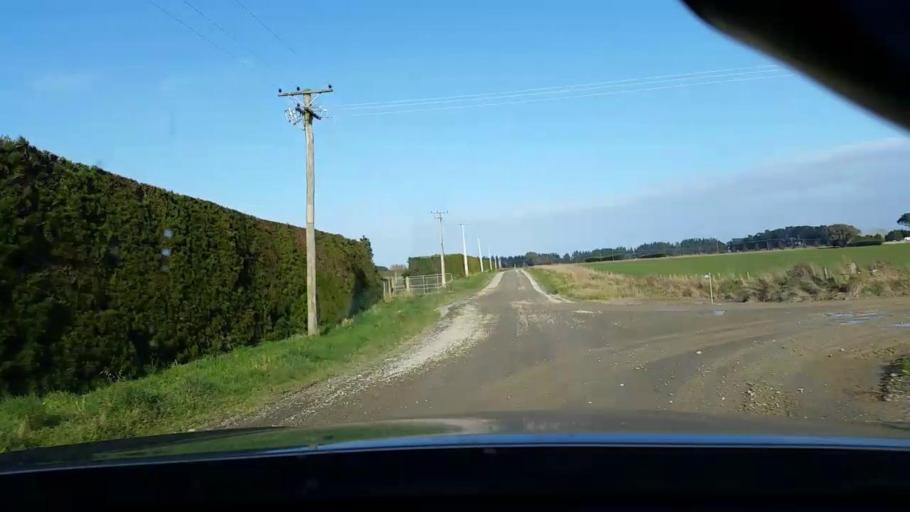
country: NZ
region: Southland
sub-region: Invercargill City
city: Invercargill
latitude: -46.2905
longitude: 168.2947
